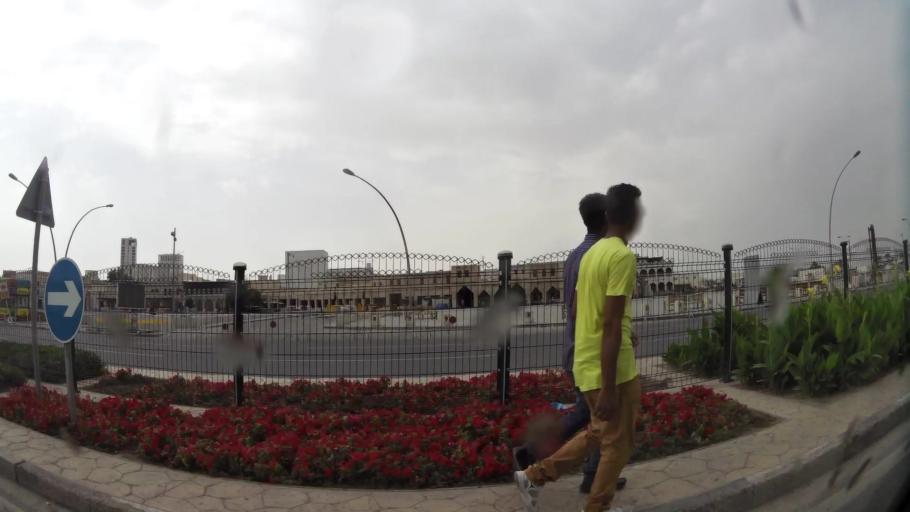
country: QA
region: Baladiyat ad Dawhah
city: Doha
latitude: 25.2890
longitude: 51.5346
